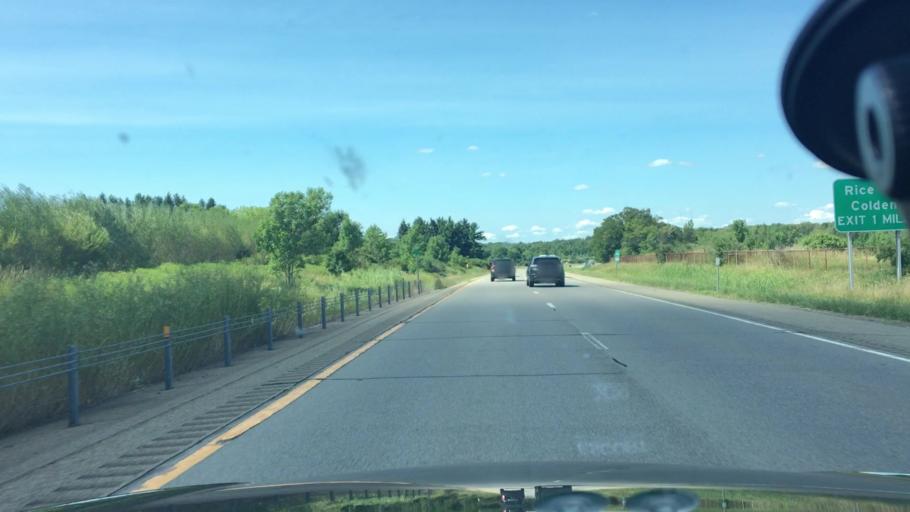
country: US
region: New York
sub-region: Erie County
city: North Boston
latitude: 42.6123
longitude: -78.7593
